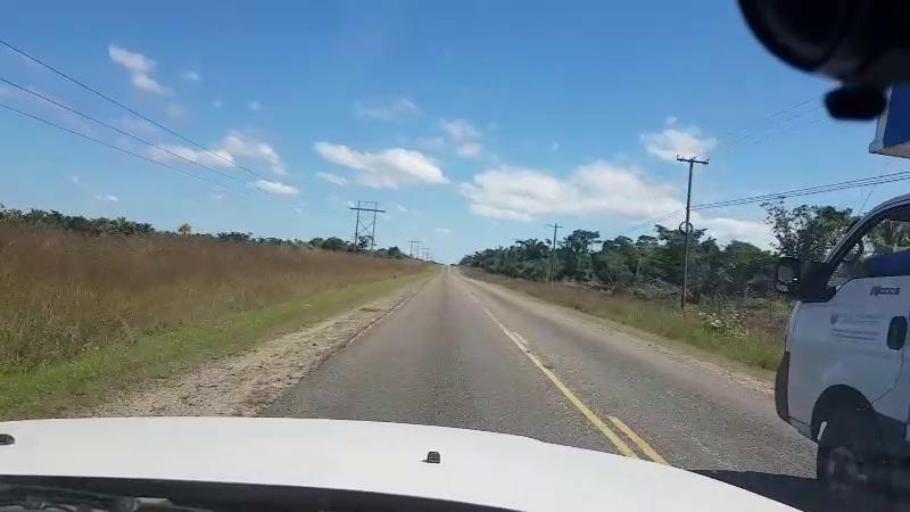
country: BZ
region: Cayo
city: Belmopan
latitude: 17.2767
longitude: -88.7364
